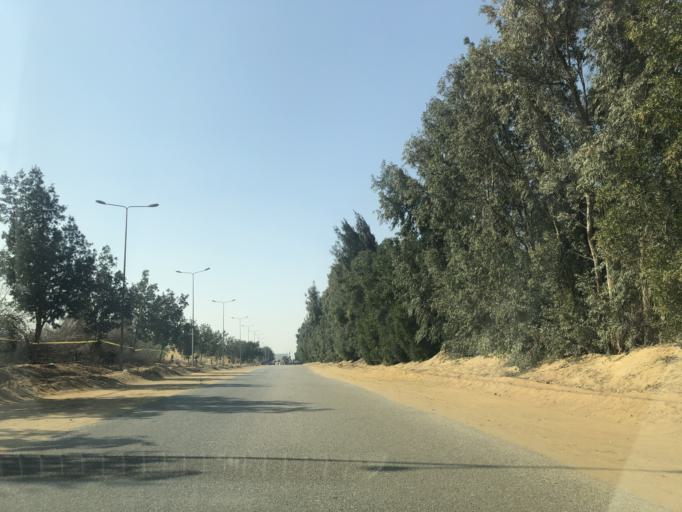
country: EG
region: Al Jizah
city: Madinat Sittah Uktubar
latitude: 29.9604
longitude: 31.0052
